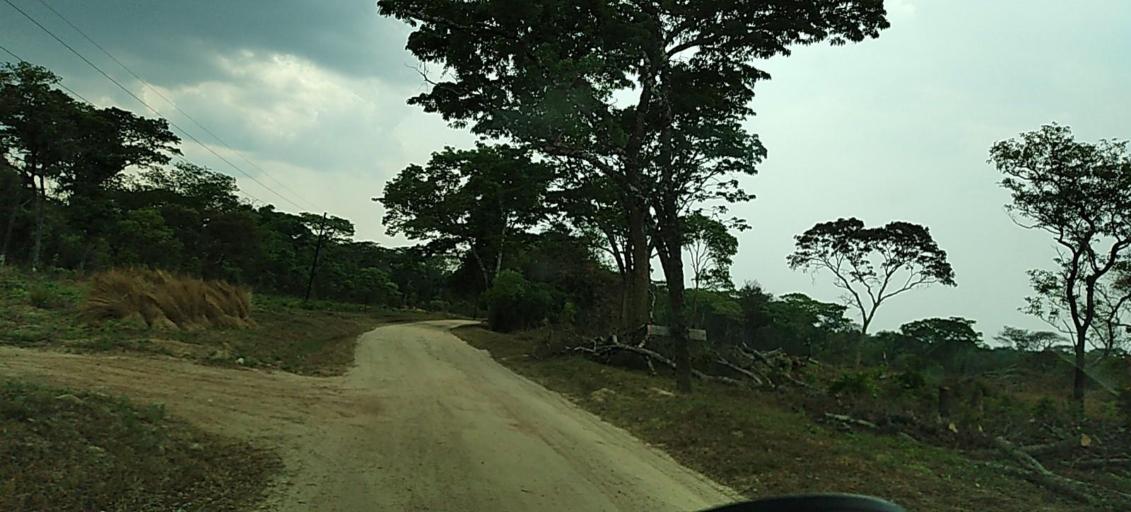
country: ZM
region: North-Western
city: Solwezi
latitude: -12.7699
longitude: 26.4658
